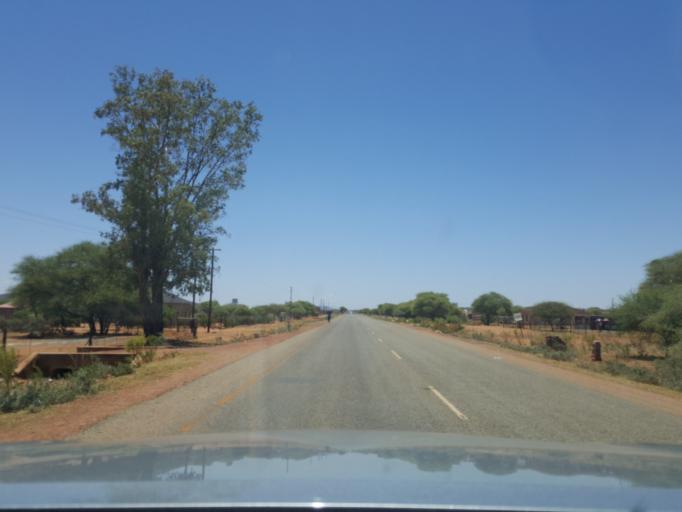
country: BW
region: South East
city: Ramotswa
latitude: -24.9647
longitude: 25.8963
